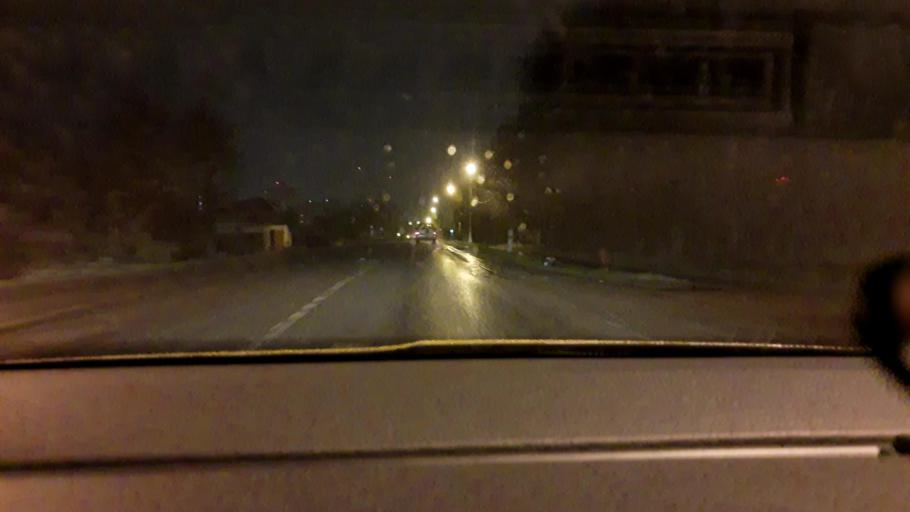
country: RU
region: Moskovskaya
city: Shchelkovo
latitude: 55.9312
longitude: 37.9815
